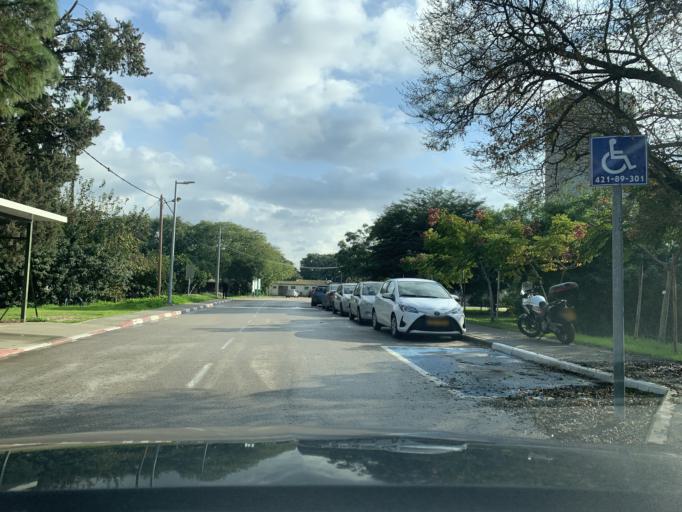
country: IL
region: Central District
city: Rosh Ha'Ayin
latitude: 32.0971
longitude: 34.9222
